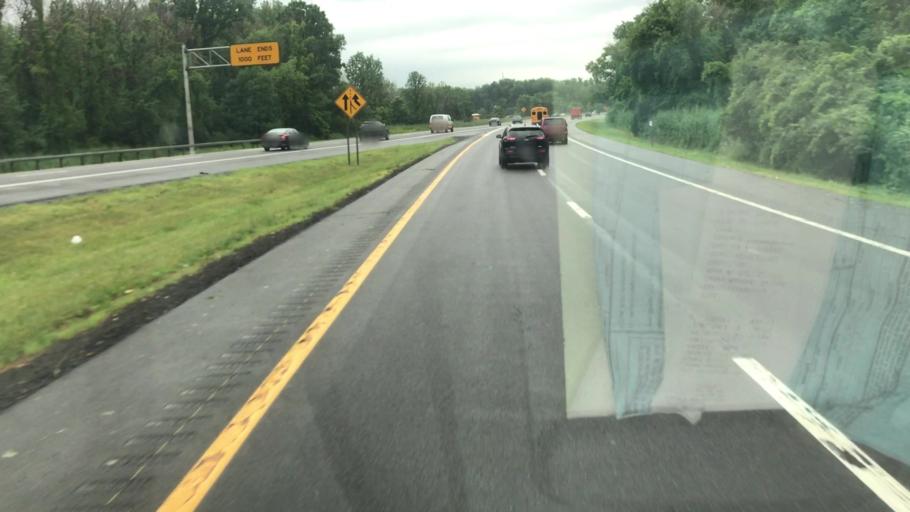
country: US
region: New York
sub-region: Onondaga County
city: East Syracuse
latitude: 43.0507
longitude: -76.0531
